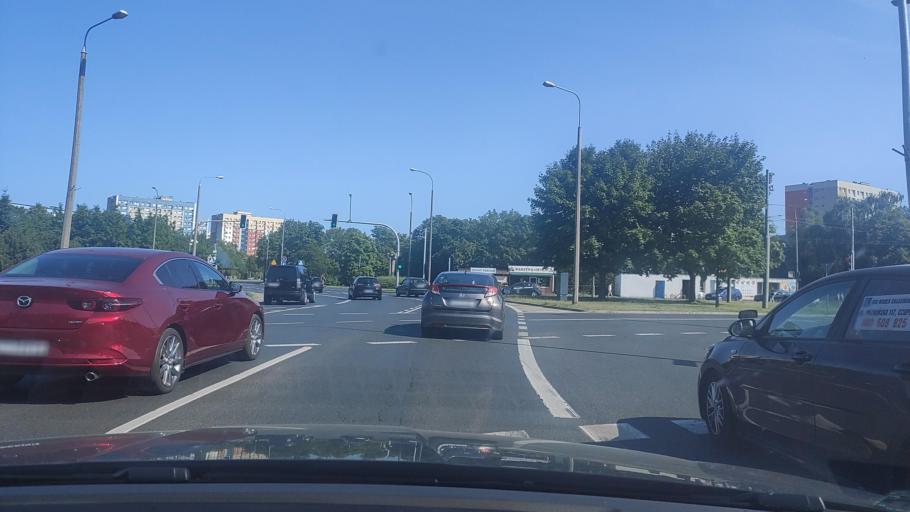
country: PL
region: Greater Poland Voivodeship
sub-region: Poznan
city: Poznan
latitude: 52.4348
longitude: 16.9376
